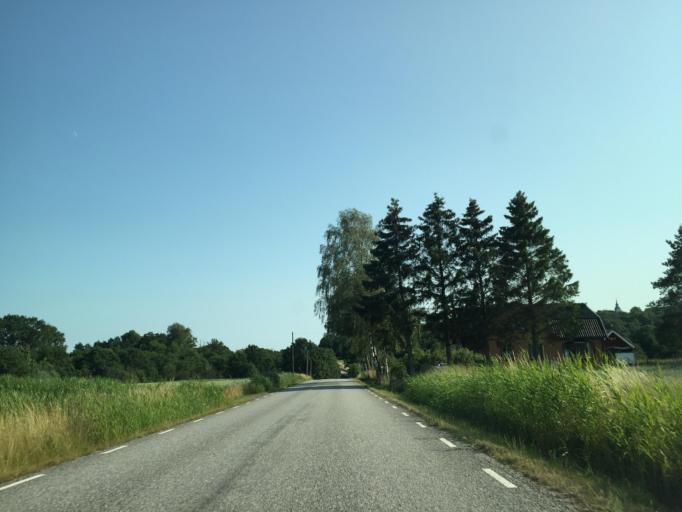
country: SE
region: Vaestra Goetaland
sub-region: Lilla Edets Kommun
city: Lilla Edet
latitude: 58.1894
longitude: 12.1174
